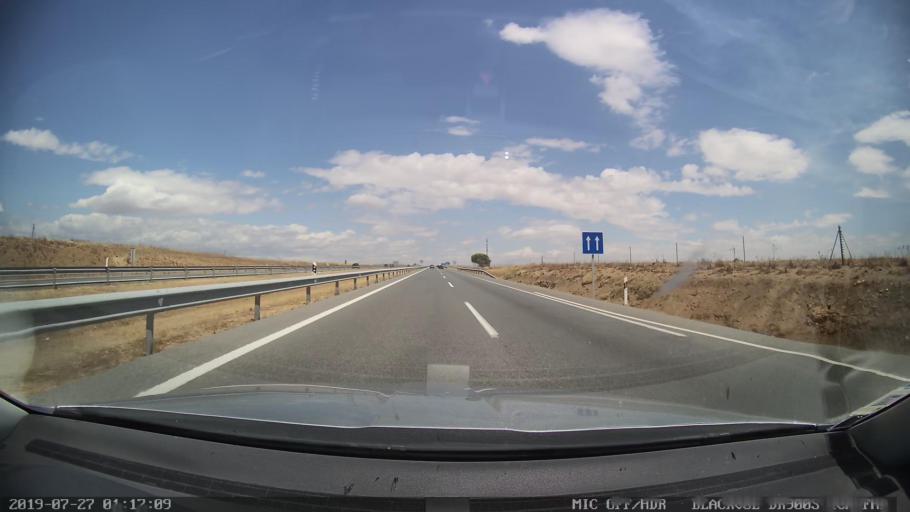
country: ES
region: Castille-La Mancha
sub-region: Province of Toledo
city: Maqueda
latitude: 40.0745
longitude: -4.3603
